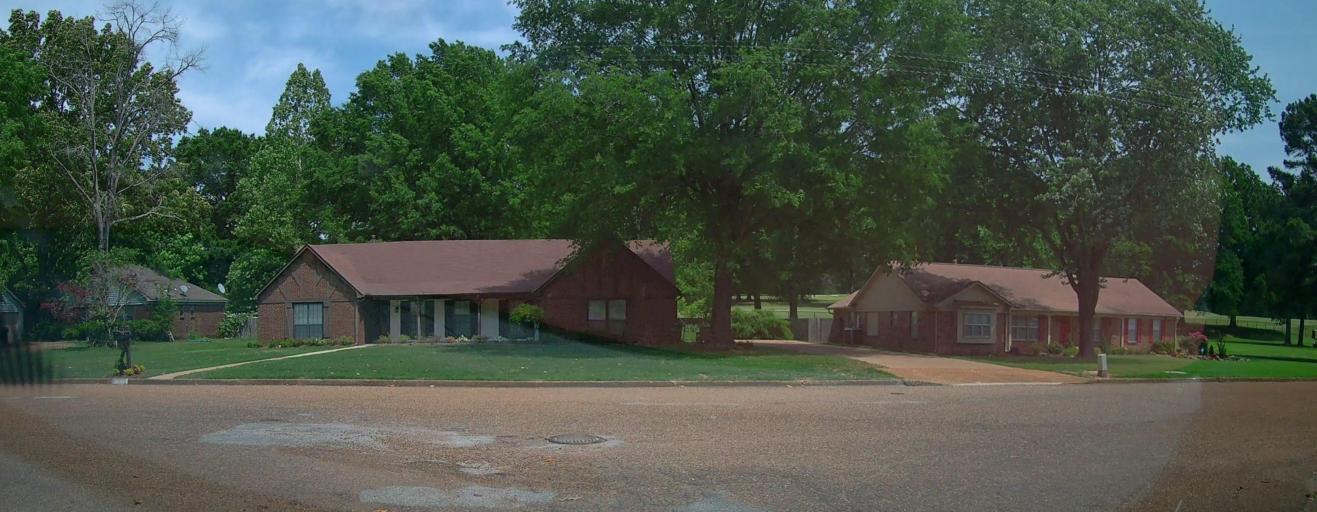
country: US
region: Tennessee
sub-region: Shelby County
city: Germantown
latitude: 35.0440
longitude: -89.7877
